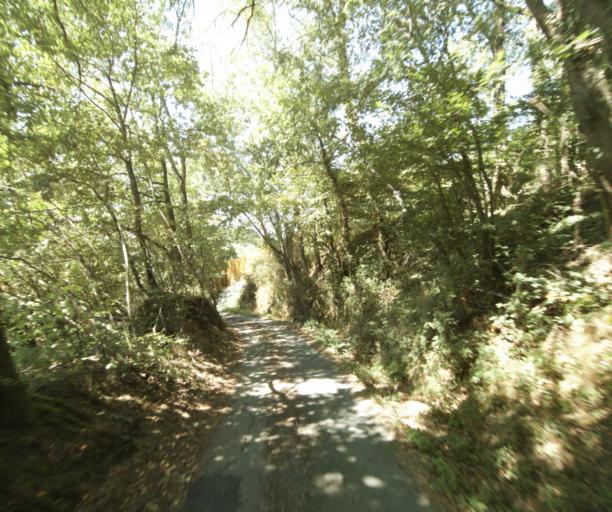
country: FR
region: Rhone-Alpes
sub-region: Departement du Rhone
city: Courzieu
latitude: 45.7504
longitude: 4.6025
